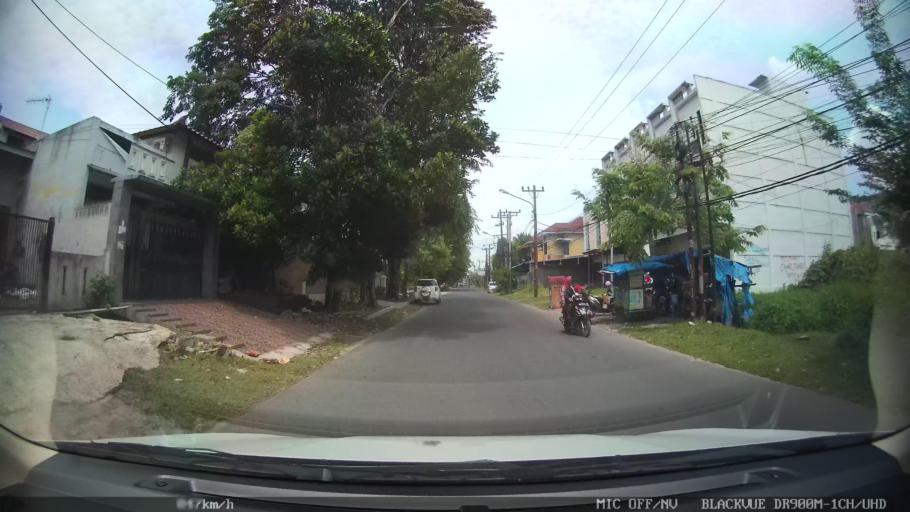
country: ID
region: North Sumatra
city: Sunggal
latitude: 3.5550
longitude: 98.6376
